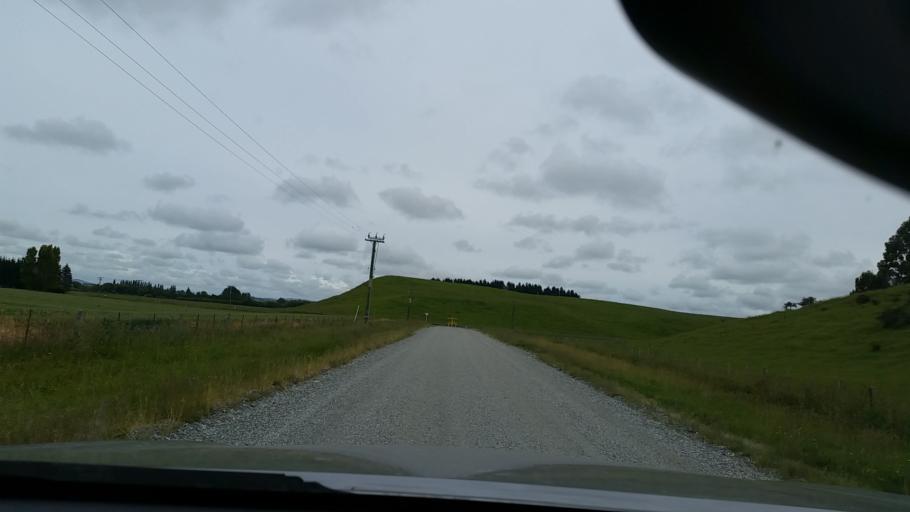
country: NZ
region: Southland
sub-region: Gore District
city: Gore
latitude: -45.8015
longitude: 168.6653
